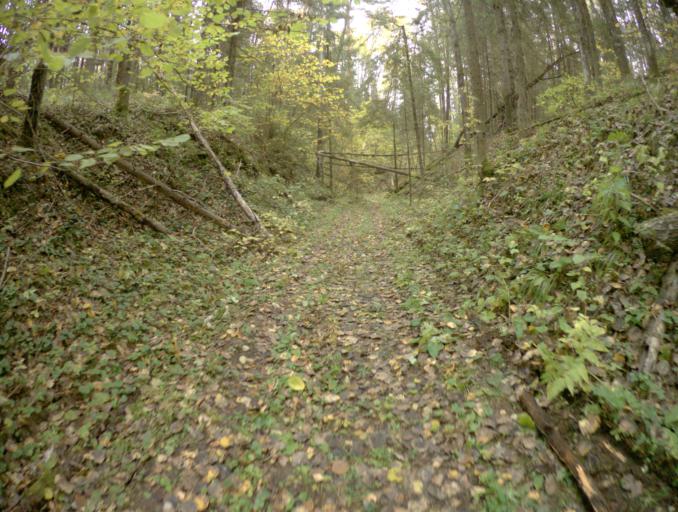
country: RU
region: Vladimir
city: Stepantsevo
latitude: 56.3098
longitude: 41.7225
